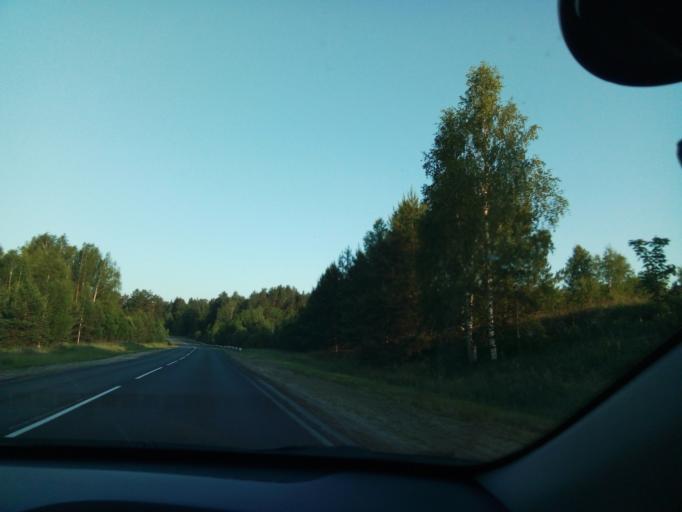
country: RU
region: Nizjnij Novgorod
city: Satis
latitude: 54.9351
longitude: 43.2263
